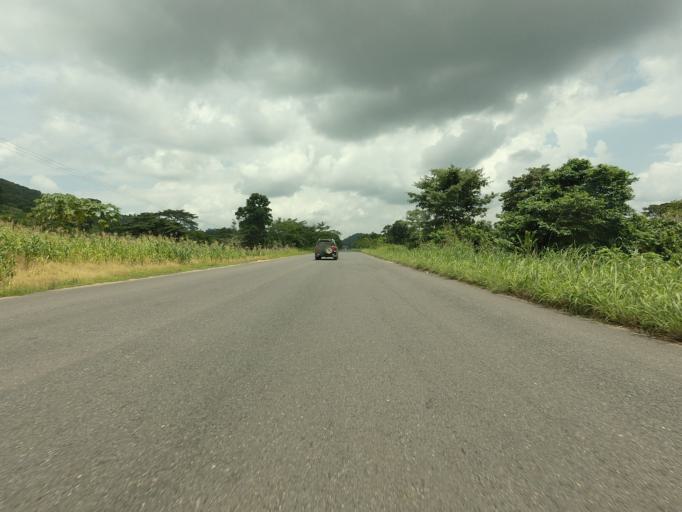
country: GH
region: Volta
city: Ho
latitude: 6.4429
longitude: 0.1737
